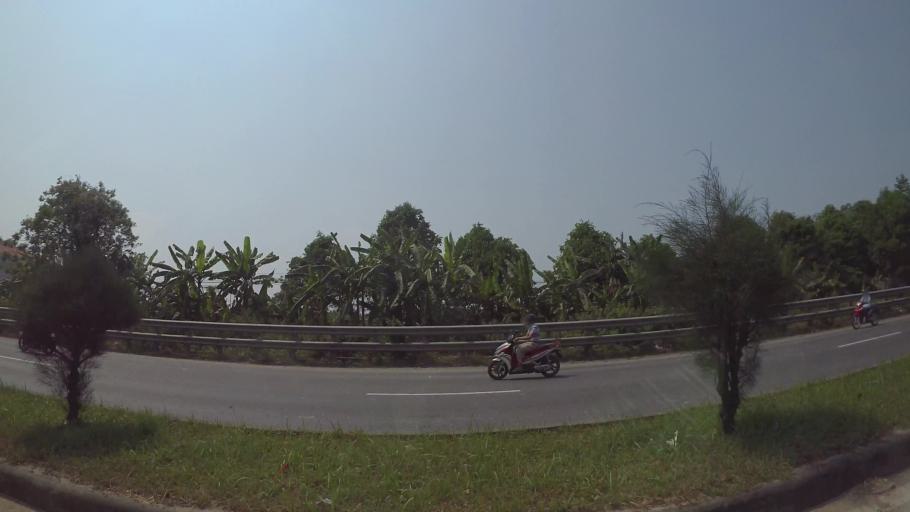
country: VN
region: Da Nang
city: Cam Le
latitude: 16.0036
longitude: 108.1905
